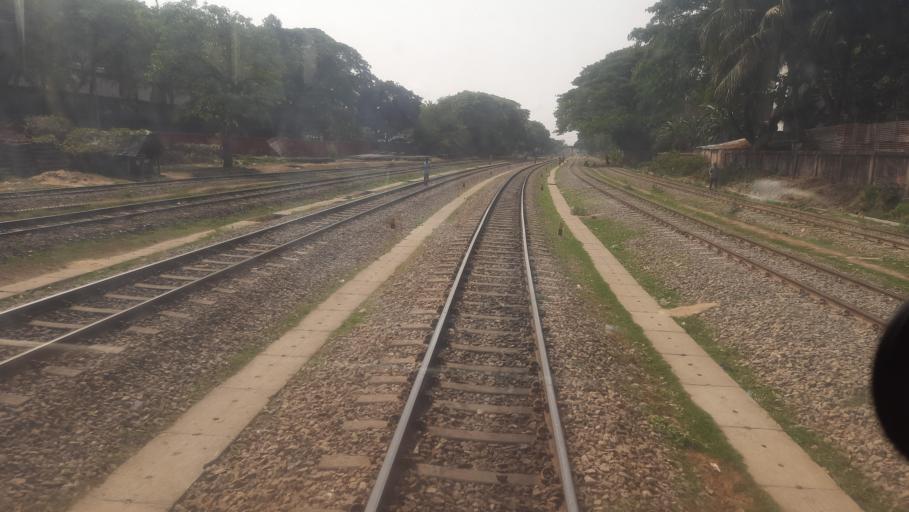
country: BD
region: Chittagong
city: Chittagong
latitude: 22.3366
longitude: 91.8204
